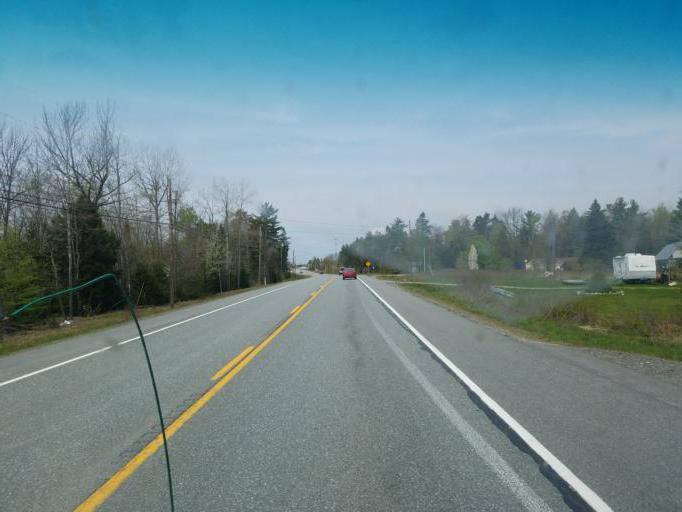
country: US
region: Maine
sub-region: Hancock County
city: Surry
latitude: 44.6111
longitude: -68.5210
